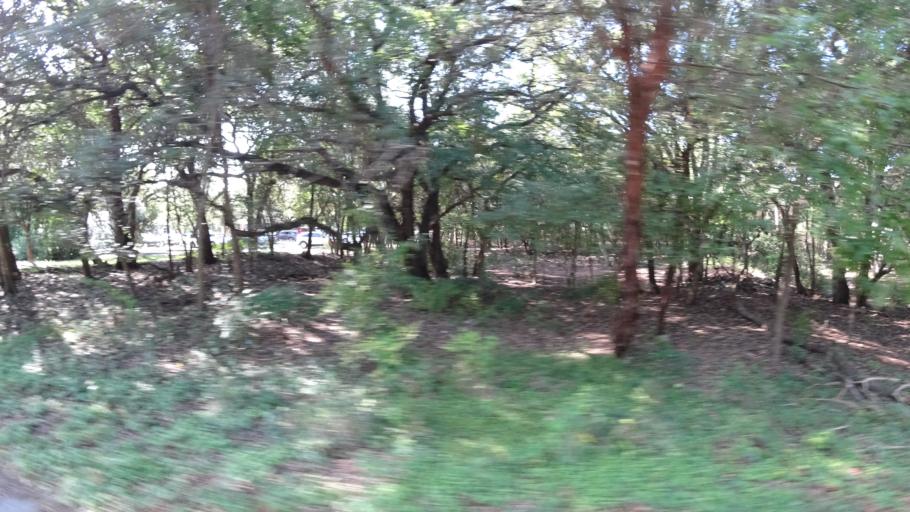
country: US
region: Texas
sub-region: Travis County
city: Rollingwood
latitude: 30.2818
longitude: -97.8070
